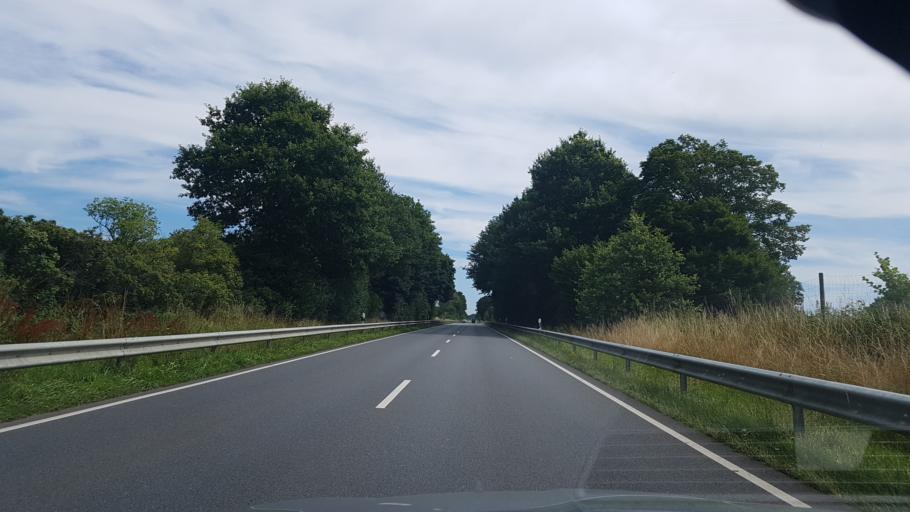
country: DE
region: Schleswig-Holstein
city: Schonbek
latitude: 54.1840
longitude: 9.9753
